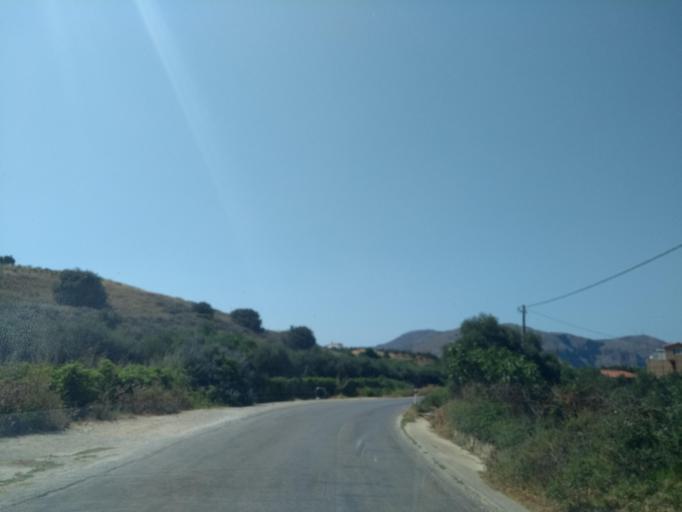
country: GR
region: Crete
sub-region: Nomos Chanias
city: Georgioupolis
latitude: 35.3554
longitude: 24.2686
